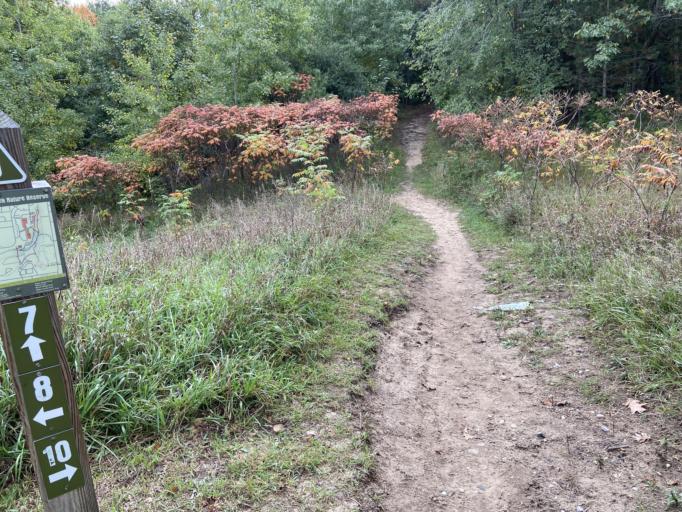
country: US
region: Michigan
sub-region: Grand Traverse County
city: Traverse City
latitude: 44.7259
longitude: -85.6309
